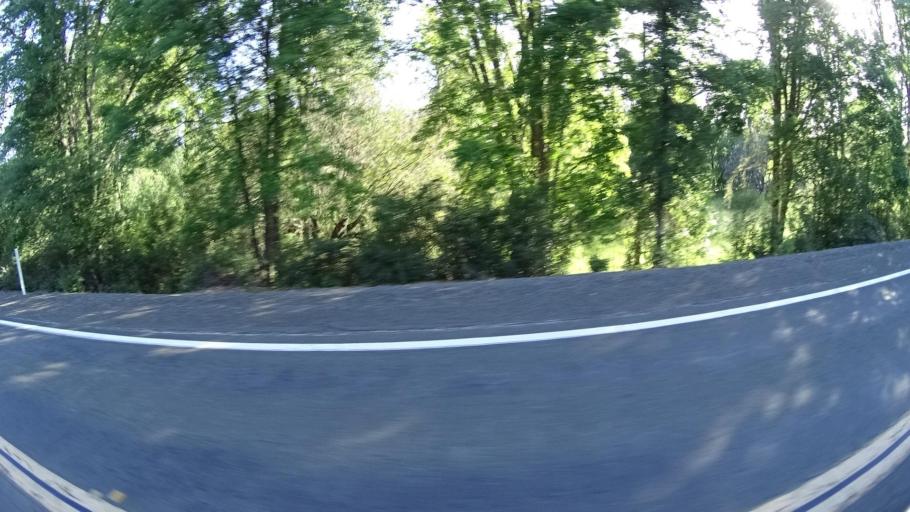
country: US
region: California
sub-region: Lake County
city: North Lakeport
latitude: 39.1060
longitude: -122.9723
